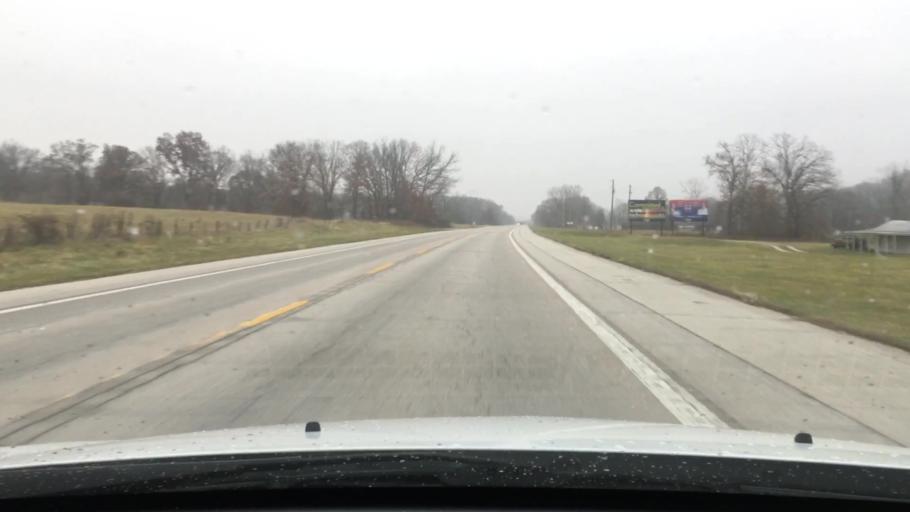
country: US
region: Missouri
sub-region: Pike County
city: Bowling Green
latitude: 39.3715
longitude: -91.1682
